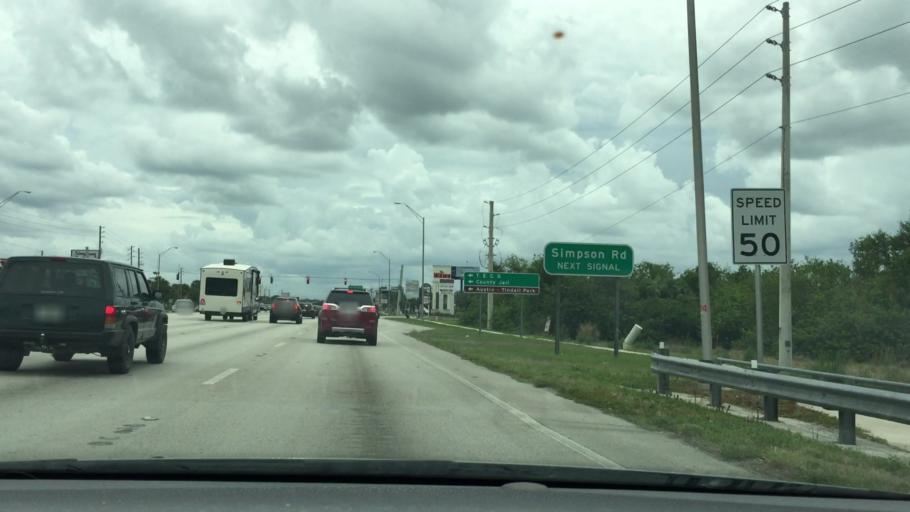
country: US
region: Florida
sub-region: Osceola County
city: Buenaventura Lakes
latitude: 28.2900
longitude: -81.3603
